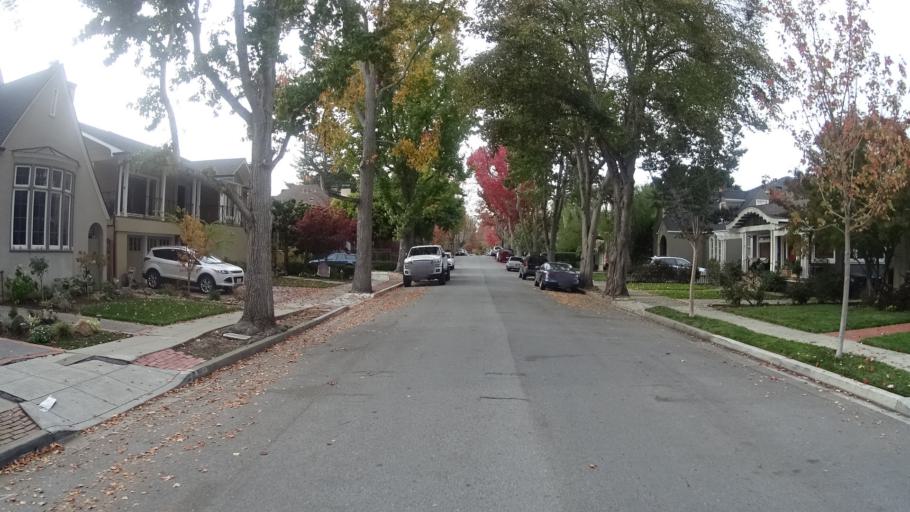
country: US
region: California
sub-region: San Mateo County
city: Burlingame
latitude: 37.5811
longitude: -122.3663
